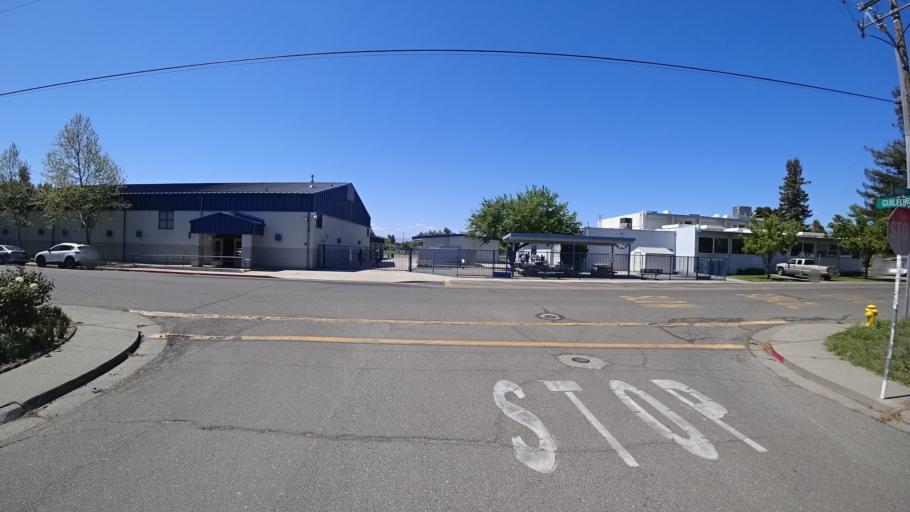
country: US
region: California
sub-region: Glenn County
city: Orland
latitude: 39.7409
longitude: -122.1920
